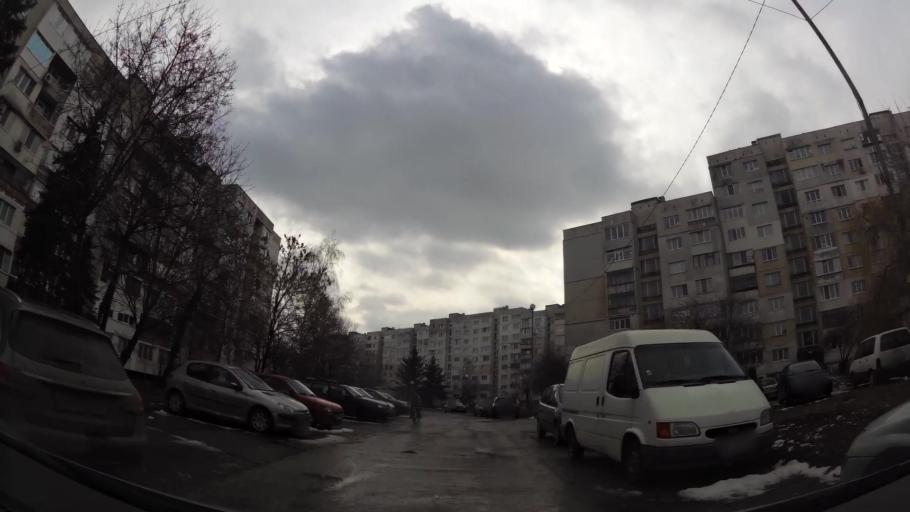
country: BG
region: Sofiya
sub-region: Obshtina Bozhurishte
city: Bozhurishte
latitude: 42.7151
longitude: 23.2381
